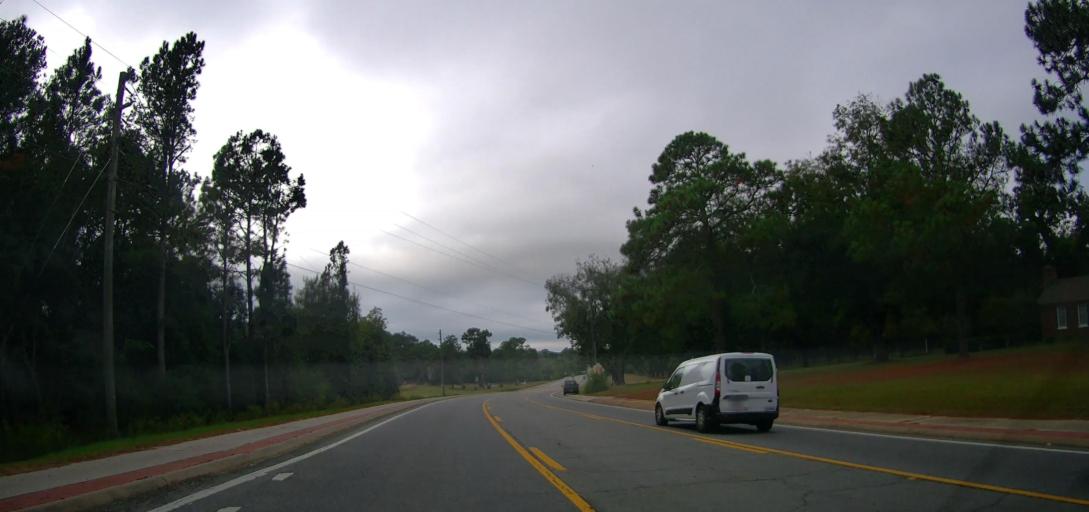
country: US
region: Georgia
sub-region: Tift County
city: Omega
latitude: 31.3363
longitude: -83.5999
